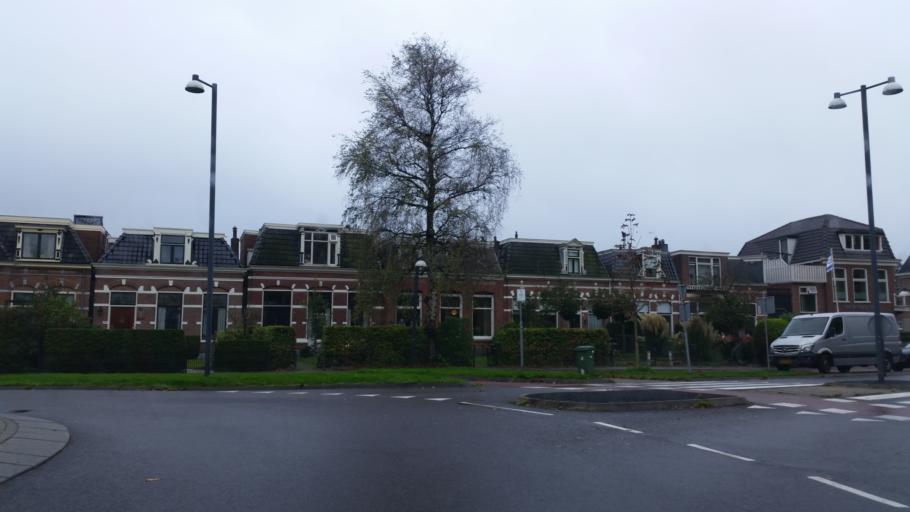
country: NL
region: Friesland
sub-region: Gemeente Leeuwarden
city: Bilgaard
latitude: 53.2071
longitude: 5.7944
